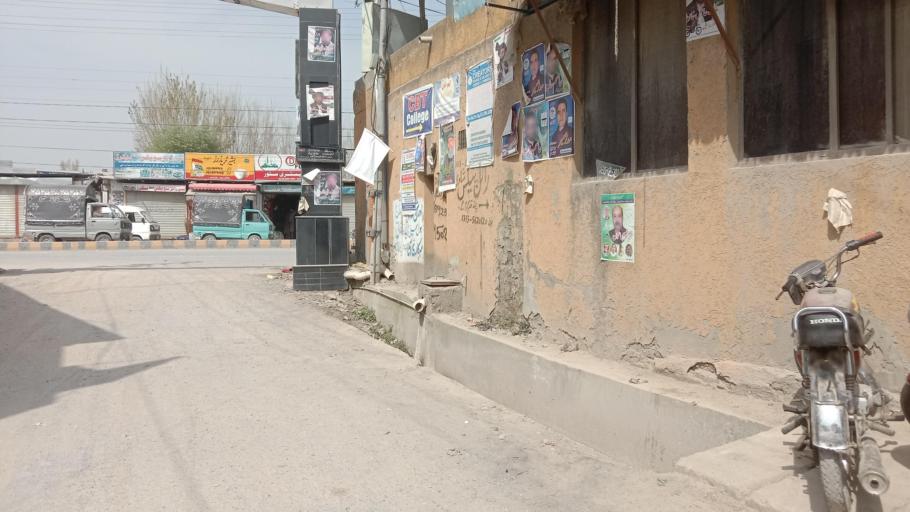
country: PK
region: Khyber Pakhtunkhwa
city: Abbottabad
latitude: 34.1576
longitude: 73.2592
